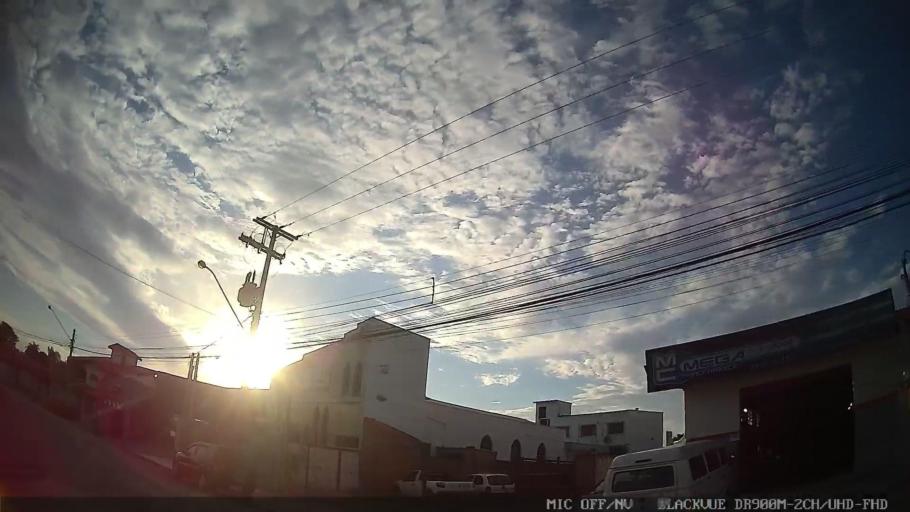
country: BR
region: Sao Paulo
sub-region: Salto
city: Salto
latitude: -23.1938
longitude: -47.2775
